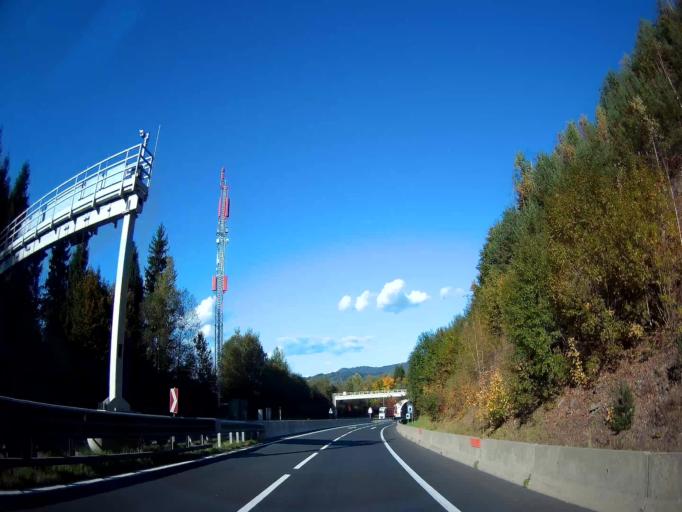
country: AT
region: Carinthia
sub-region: Klagenfurt am Woerthersee
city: Klagenfurt am Woerthersee
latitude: 46.6469
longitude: 14.2527
